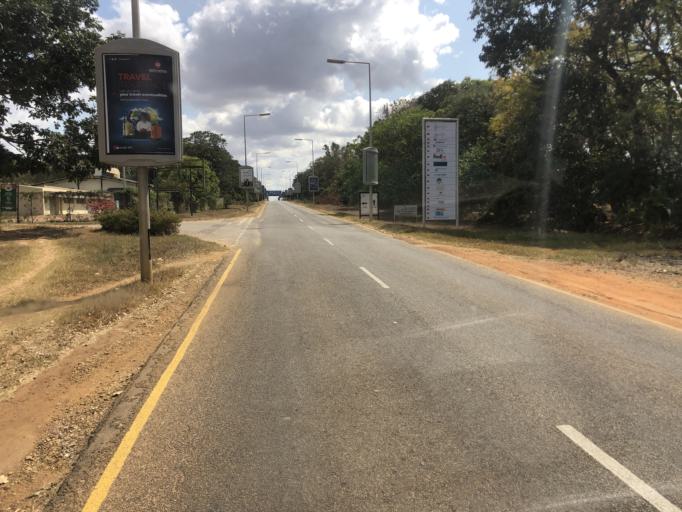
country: MW
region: Central Region
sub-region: Lilongwe District
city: Lilongwe
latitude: -13.7844
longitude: 33.7872
